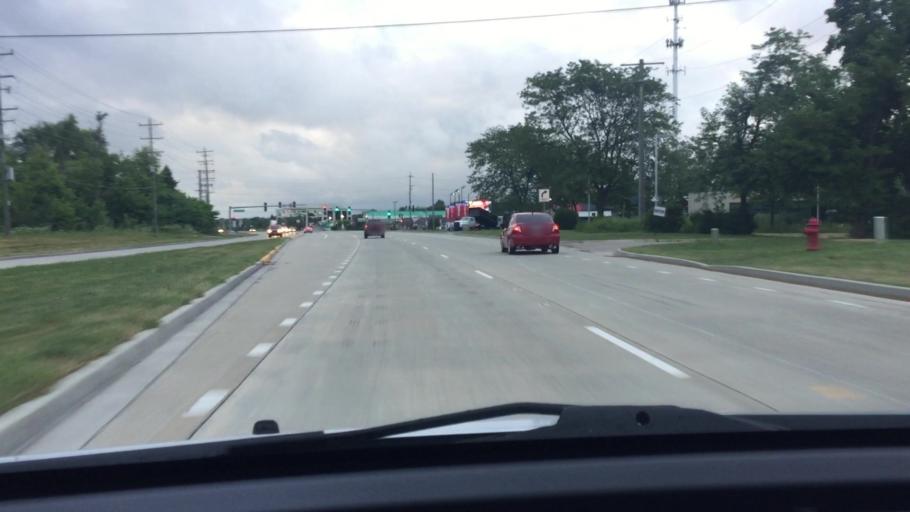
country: US
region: Illinois
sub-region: McHenry County
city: McHenry
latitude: 42.3189
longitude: -88.2751
